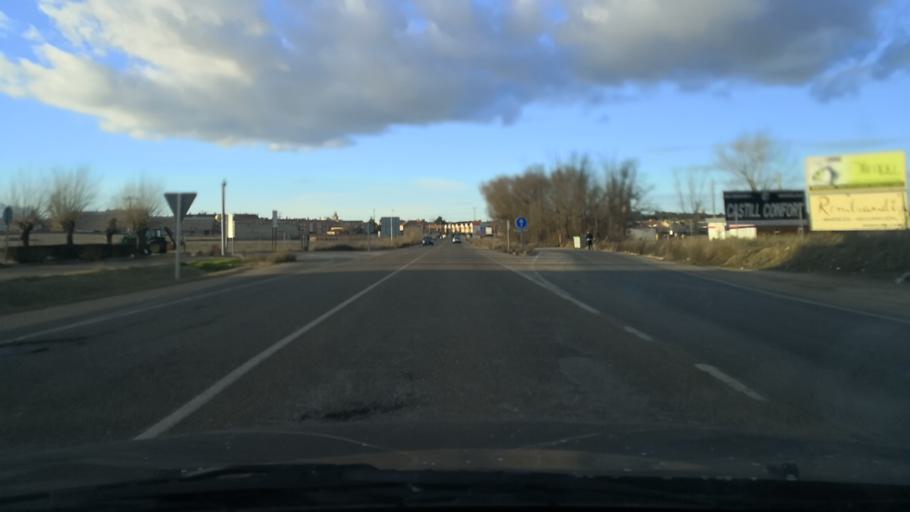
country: ES
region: Castille and Leon
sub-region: Provincia de Valladolid
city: Medina del Campo
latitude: 41.2964
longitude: -4.9041
